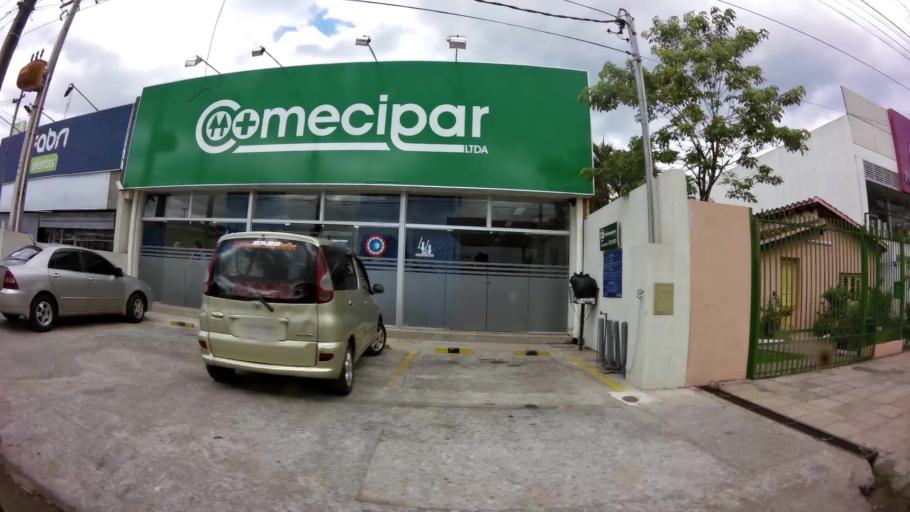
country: PY
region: Central
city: San Lorenzo
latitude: -25.2660
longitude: -57.5010
